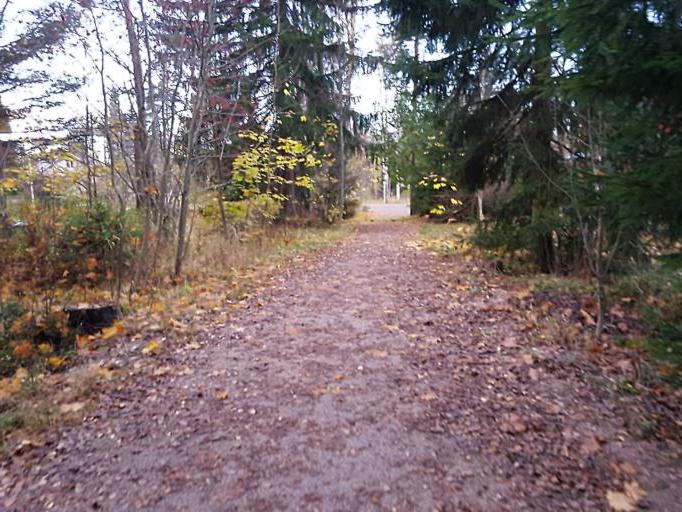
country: FI
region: Uusimaa
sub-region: Helsinki
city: Teekkarikylae
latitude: 60.2547
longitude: 24.8912
